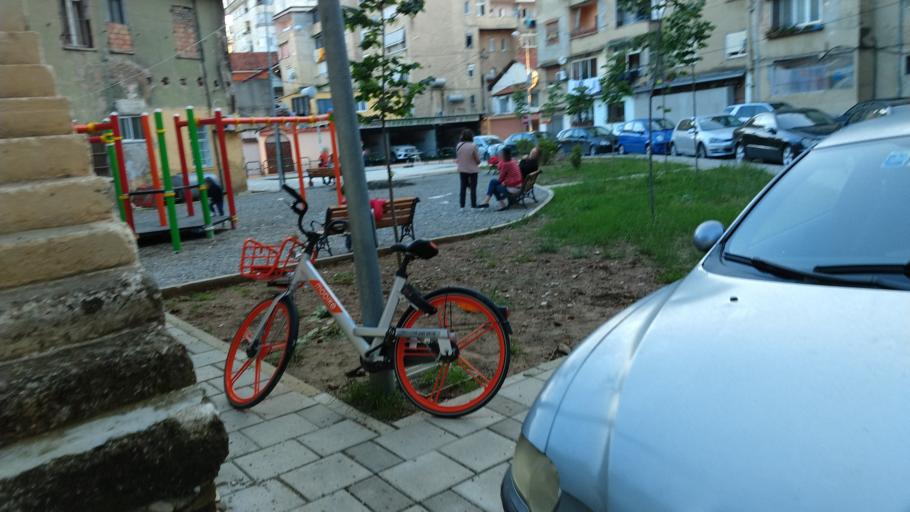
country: AL
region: Tirane
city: Tirana
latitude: 41.3316
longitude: 19.8066
